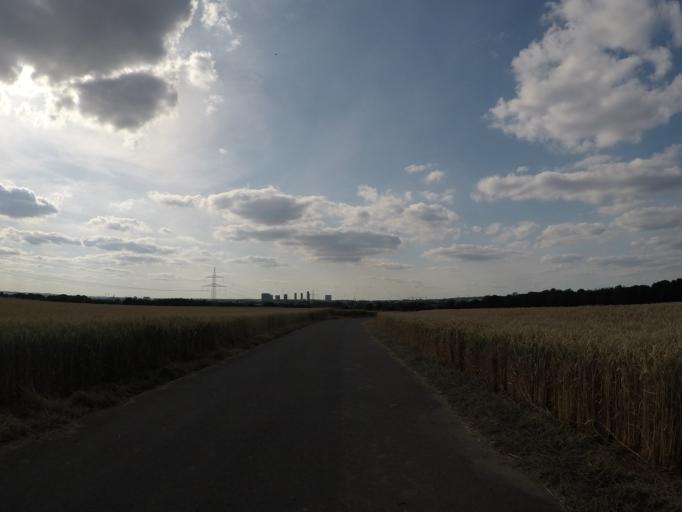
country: LU
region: Luxembourg
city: Itzig
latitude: 49.6007
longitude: 6.1804
